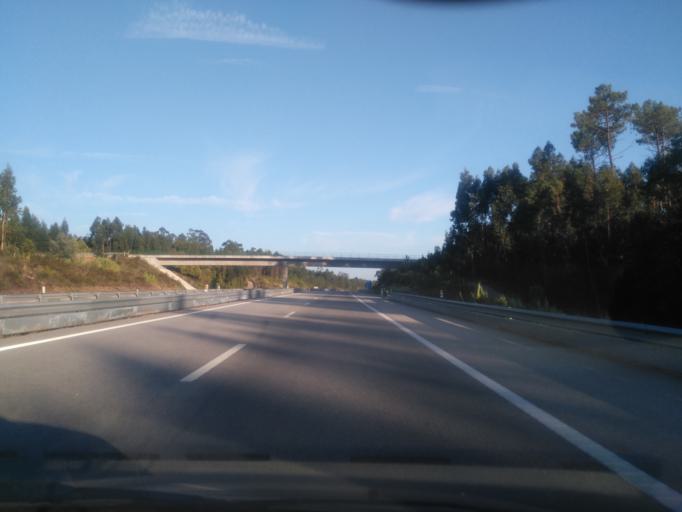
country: PT
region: Coimbra
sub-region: Figueira da Foz
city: Alhadas
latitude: 40.1716
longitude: -8.7914
